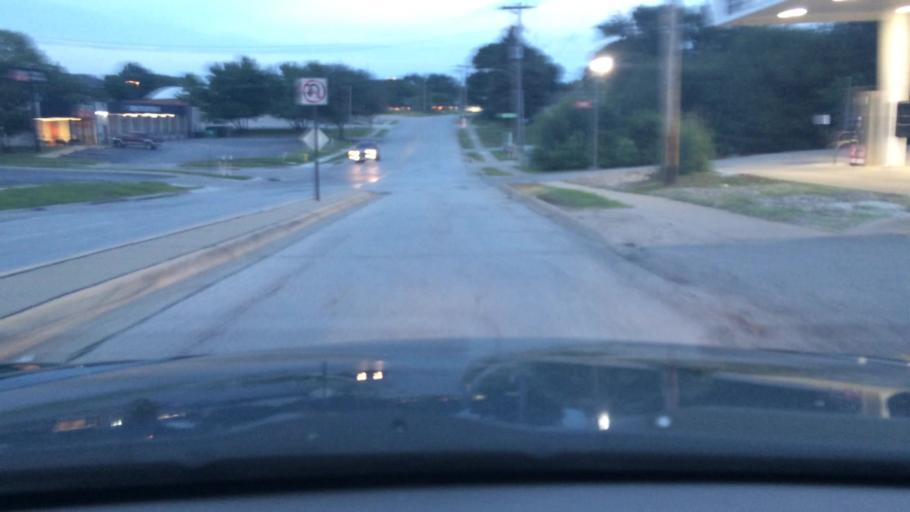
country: US
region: Nebraska
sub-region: Sarpy County
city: La Vista
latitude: 41.1876
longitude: -96.0426
